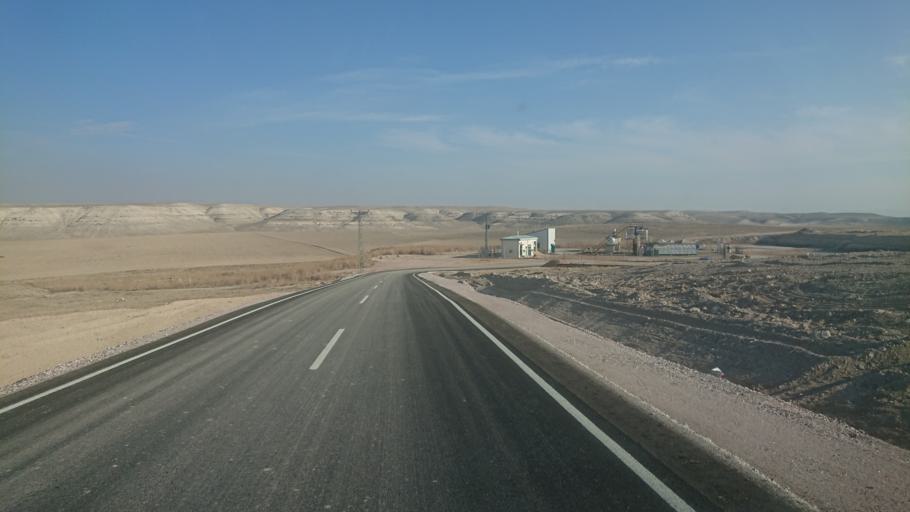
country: TR
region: Aksaray
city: Sultanhani
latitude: 38.0890
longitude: 33.6139
